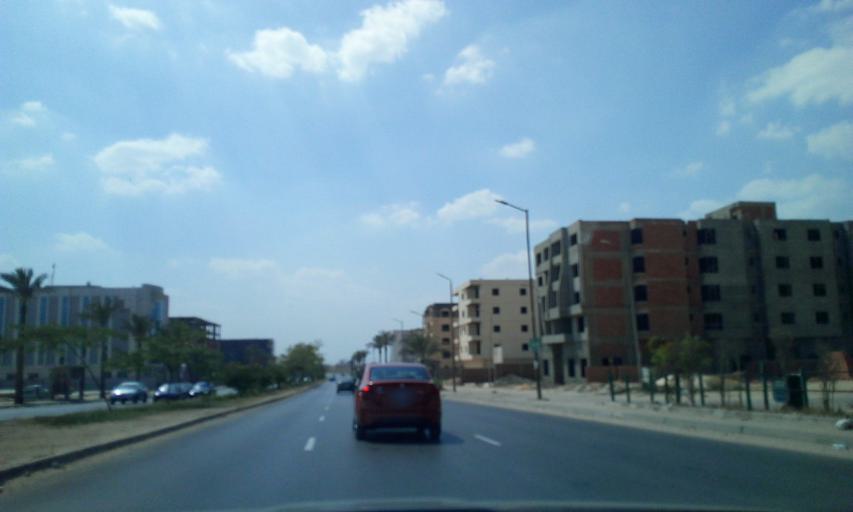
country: EG
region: Muhafazat al Qalyubiyah
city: Al Khankah
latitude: 30.0913
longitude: 31.3760
